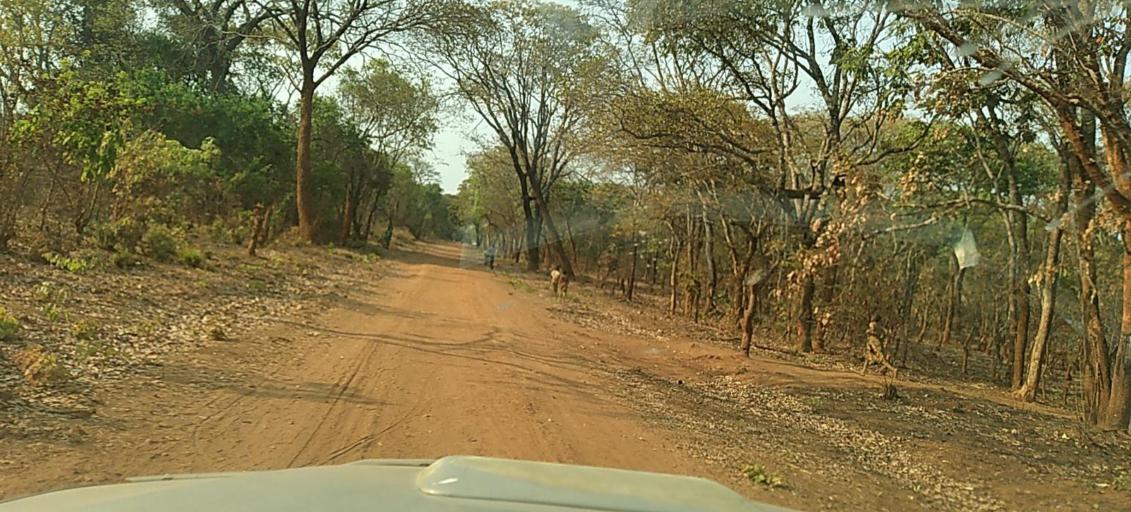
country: ZM
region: North-Western
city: Kasempa
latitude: -13.3118
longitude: 26.5522
